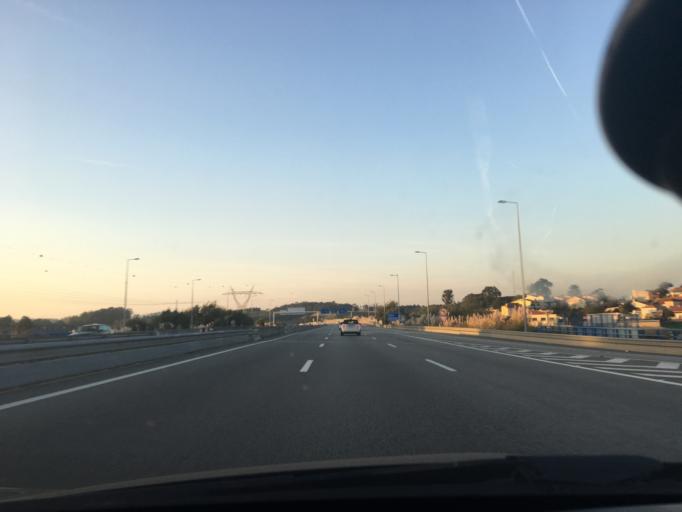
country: PT
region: Porto
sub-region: Matosinhos
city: Guifoes
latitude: 41.2113
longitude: -8.6524
